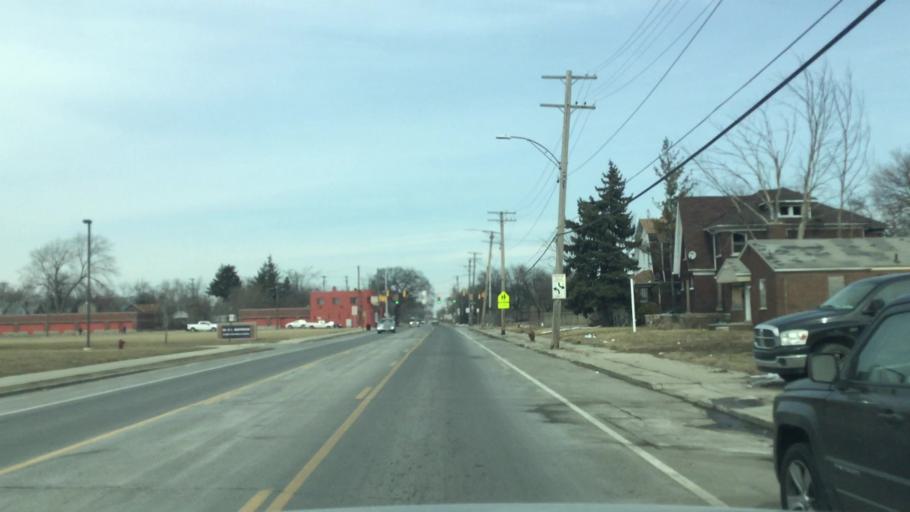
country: US
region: Michigan
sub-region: Wayne County
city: Dearborn
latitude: 42.3647
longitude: -83.1581
